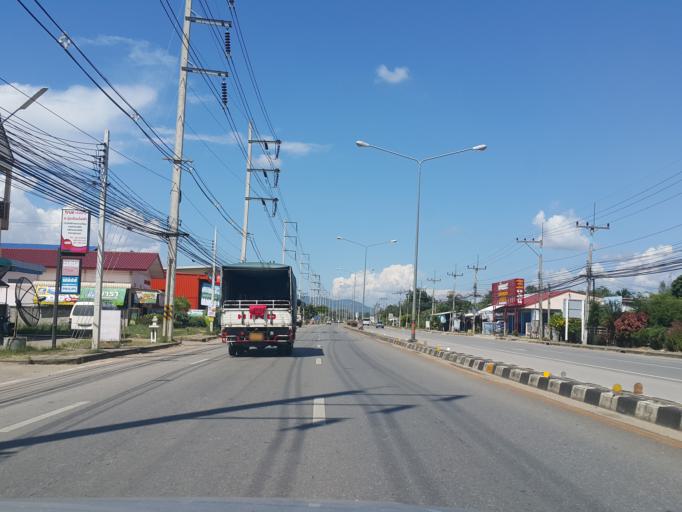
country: TH
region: Chiang Mai
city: Mae Taeng
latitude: 19.0996
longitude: 98.9358
